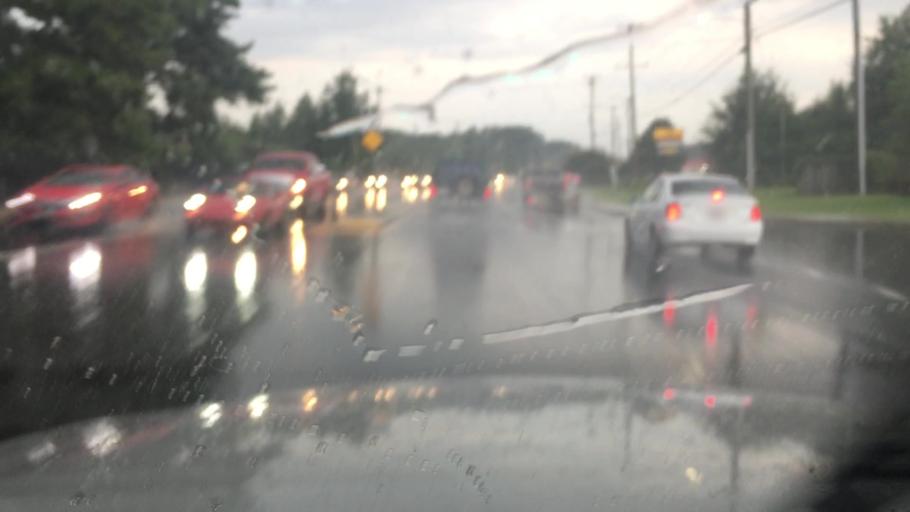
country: US
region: North Carolina
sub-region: Cumberland County
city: Fort Bragg
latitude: 35.0642
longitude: -79.0139
